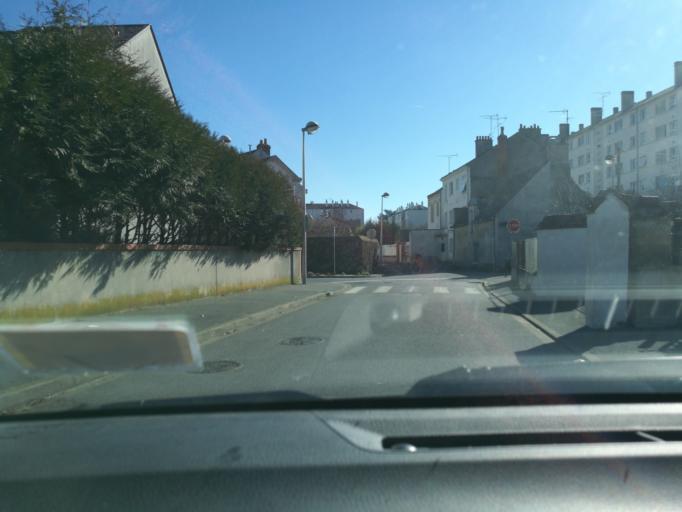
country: FR
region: Centre
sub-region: Departement du Loiret
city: Saint-Jean-le-Blanc
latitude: 47.8929
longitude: 1.9091
